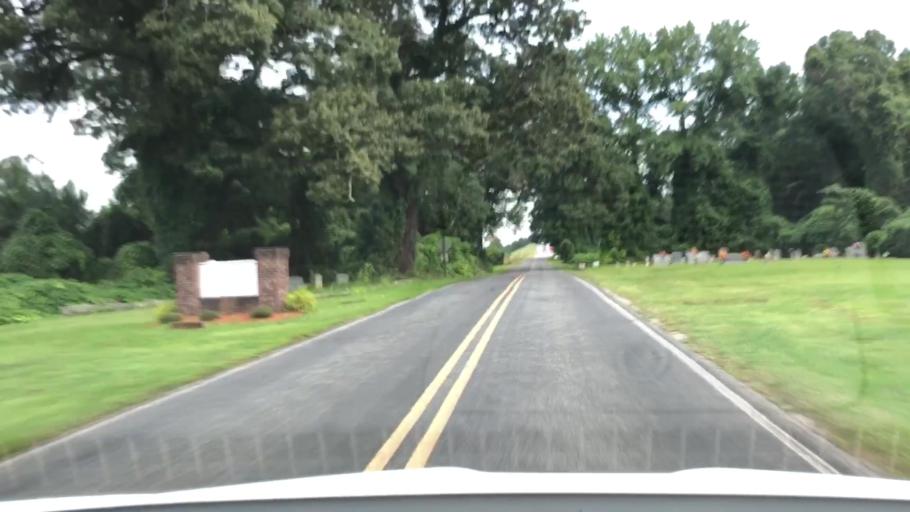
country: US
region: North Carolina
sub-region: Jones County
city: Maysville
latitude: 34.9075
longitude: -77.2336
